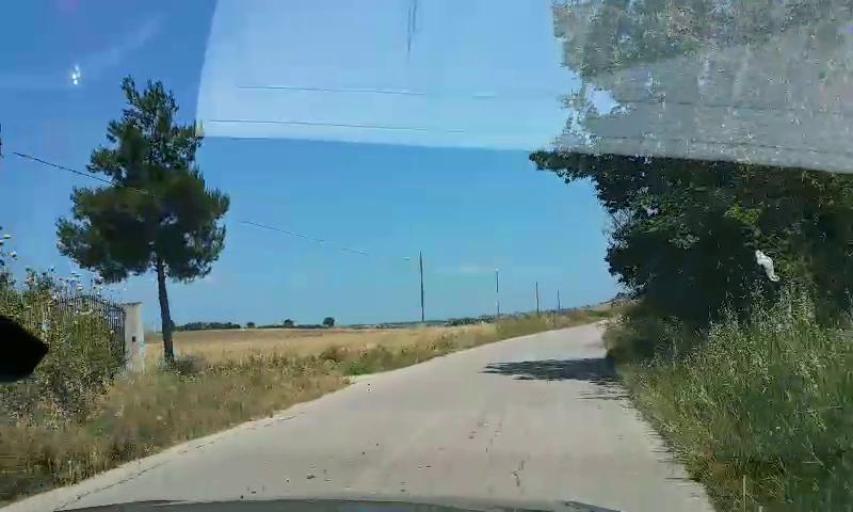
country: IT
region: Molise
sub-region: Provincia di Campobasso
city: Guglionesi
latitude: 41.9485
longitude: 14.9010
